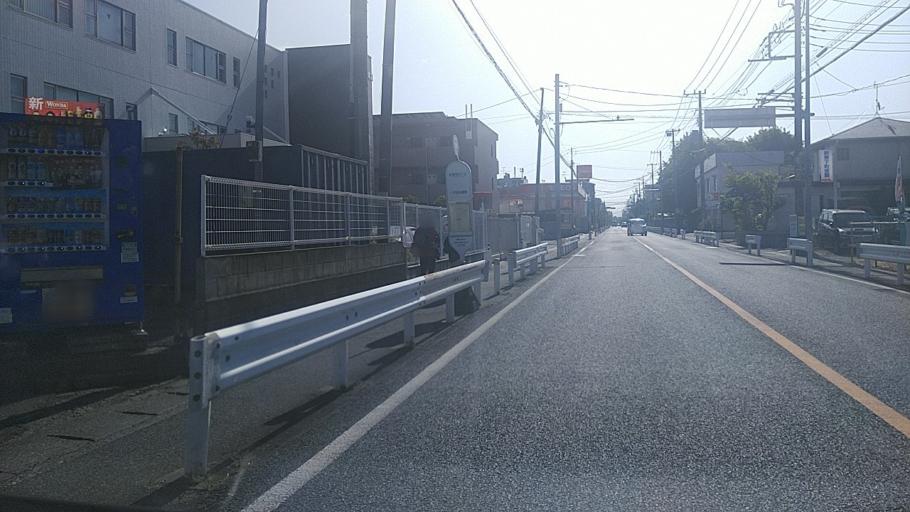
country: JP
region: Saitama
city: Shimotoda
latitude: 35.8082
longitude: 139.6635
